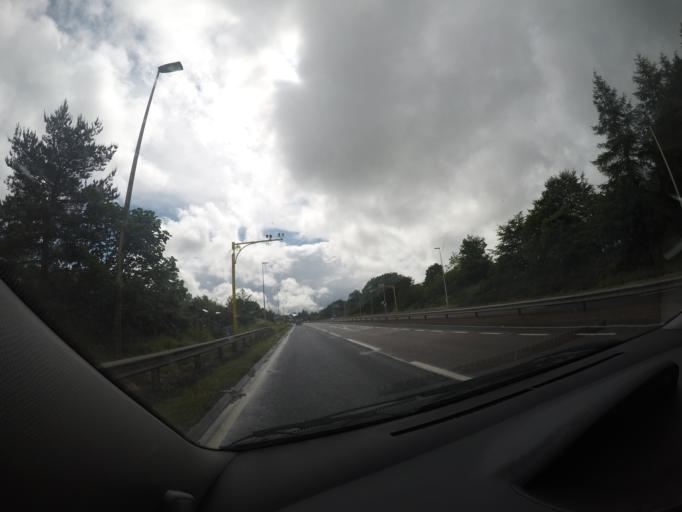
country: GB
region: Scotland
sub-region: Perth and Kinross
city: Auchterarder
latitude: 56.2837
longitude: -3.7261
